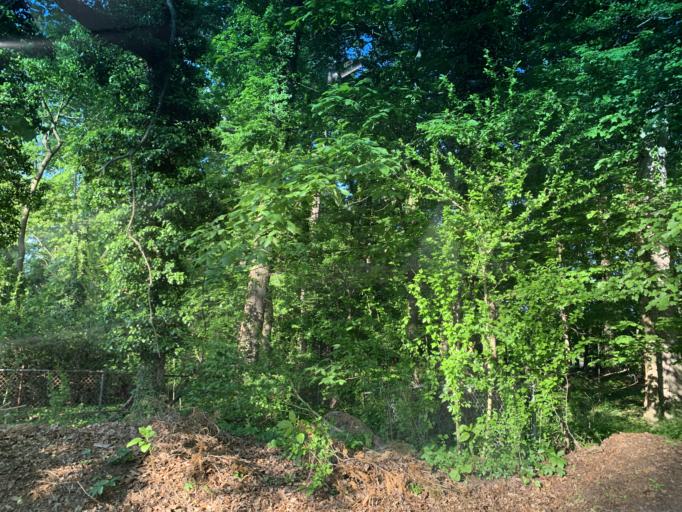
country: US
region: Maryland
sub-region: Harford County
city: Bel Air South
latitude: 39.5077
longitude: -76.2915
